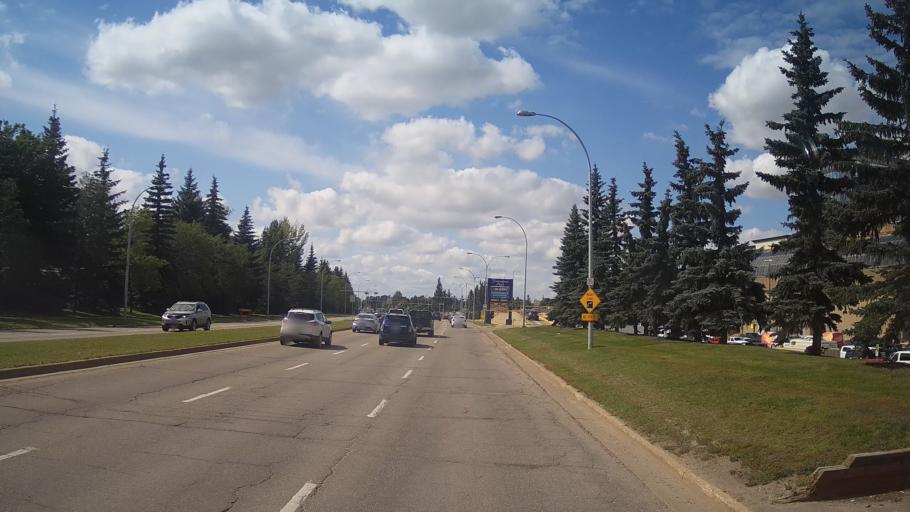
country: CA
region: Alberta
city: St. Albert
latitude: 53.5206
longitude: -113.6253
